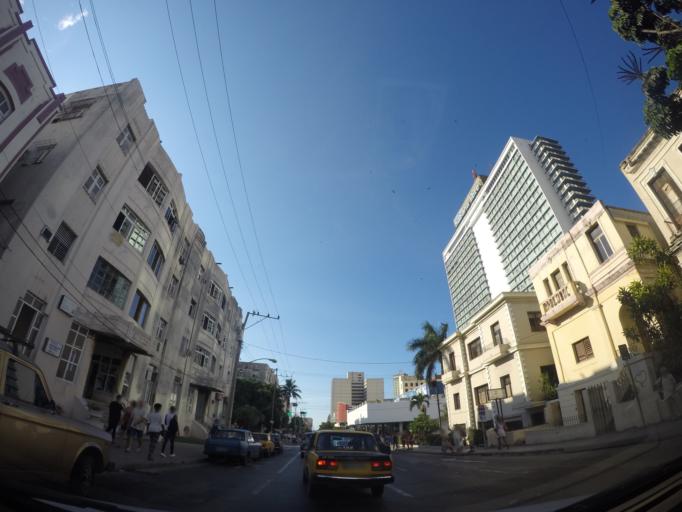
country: CU
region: La Habana
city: Havana
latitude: 23.1383
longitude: -82.3823
